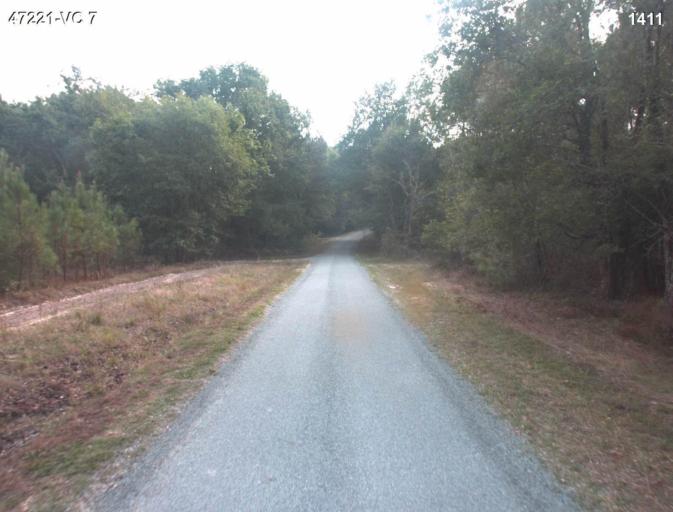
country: FR
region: Aquitaine
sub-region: Departement du Lot-et-Garonne
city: Mezin
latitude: 44.0874
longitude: 0.2247
